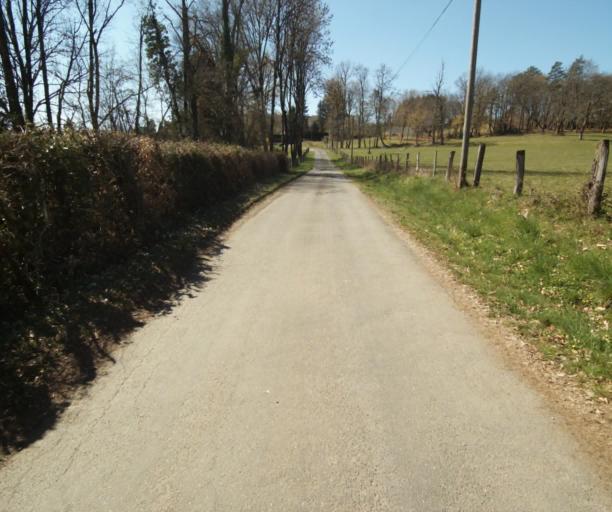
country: FR
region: Limousin
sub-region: Departement de la Correze
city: Saint-Clement
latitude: 45.3044
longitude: 1.6976
